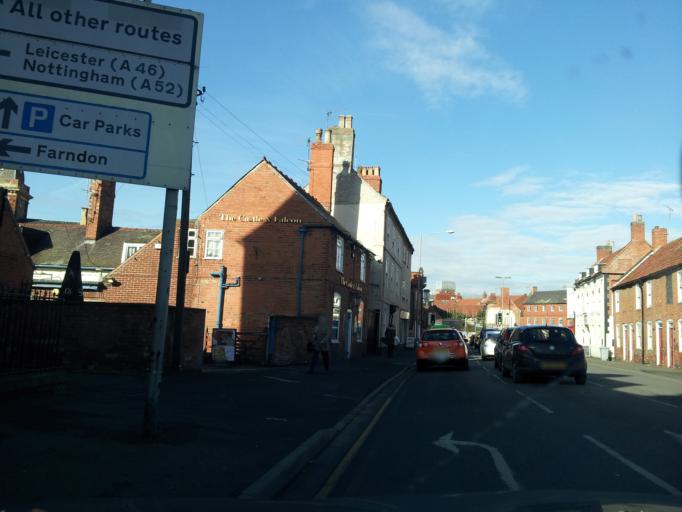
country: GB
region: England
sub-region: Nottinghamshire
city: Newark on Trent
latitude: 53.0737
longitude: -0.8091
